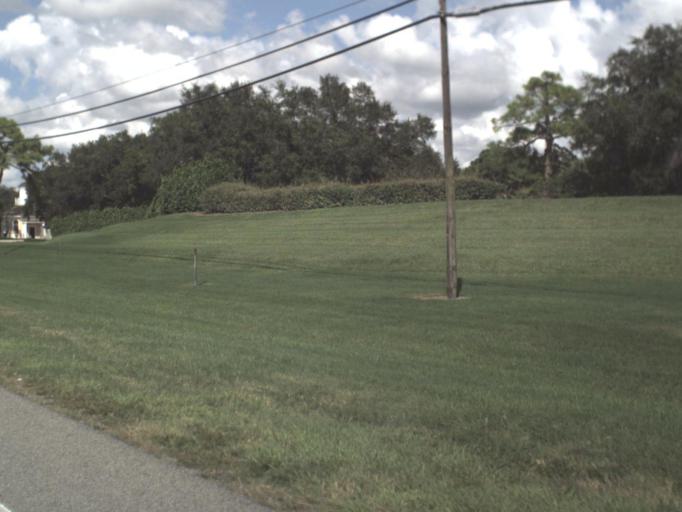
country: US
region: Florida
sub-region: Sarasota County
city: Osprey
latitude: 27.2059
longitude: -82.4902
